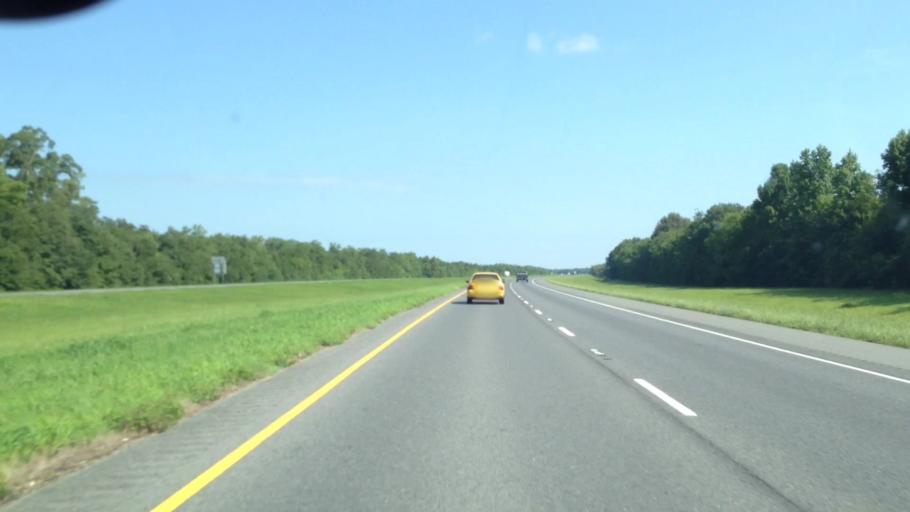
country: US
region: Louisiana
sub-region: Saint Landry Parish
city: Opelousas
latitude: 30.6675
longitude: -92.0706
